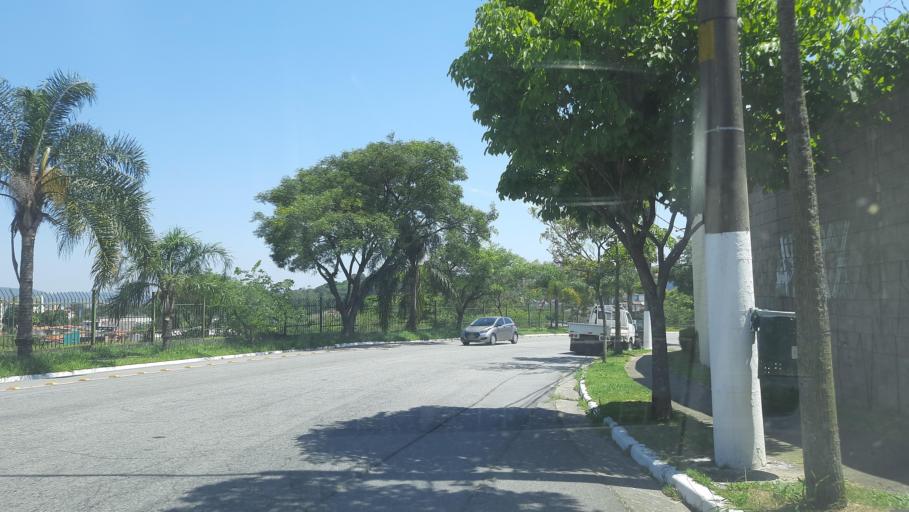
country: BR
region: Sao Paulo
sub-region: Caieiras
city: Caieiras
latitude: -23.4408
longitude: -46.7303
